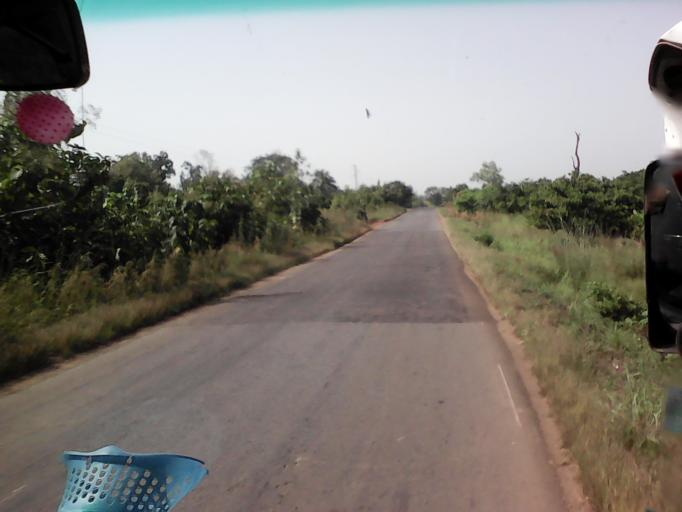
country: TG
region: Centrale
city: Sokode
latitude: 8.9104
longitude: 1.1005
